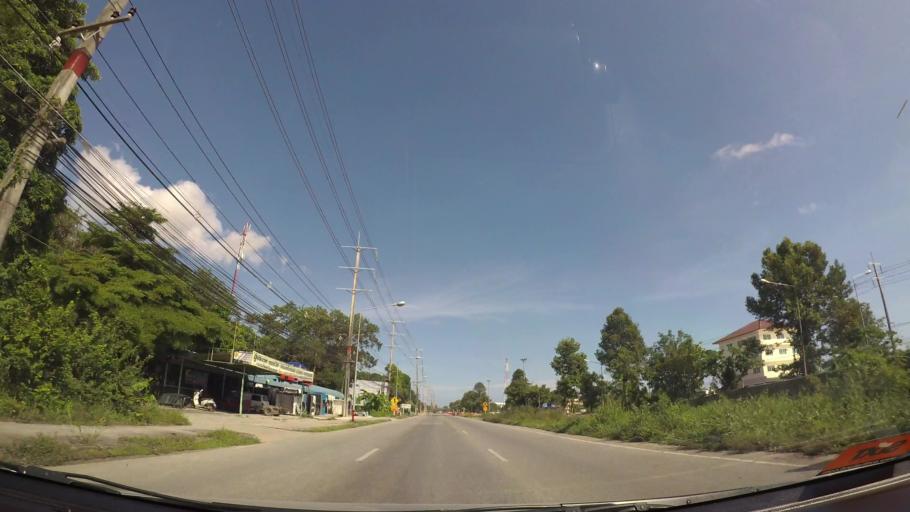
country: TH
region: Rayong
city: Rayong
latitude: 12.6819
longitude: 101.3006
